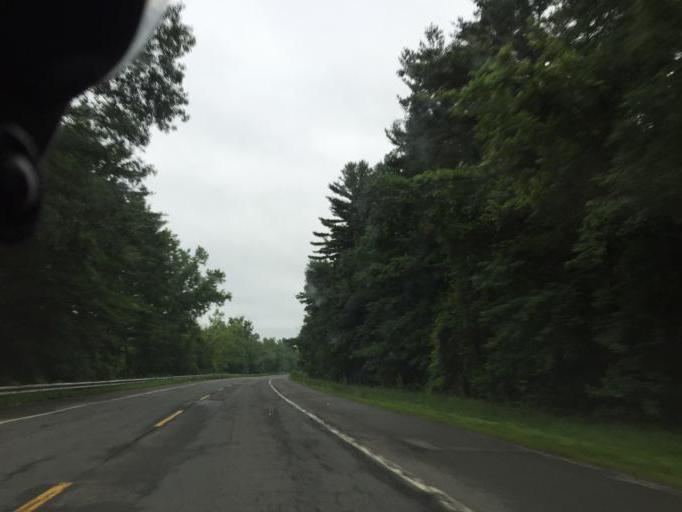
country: US
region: Massachusetts
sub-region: Berkshire County
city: Sheffield
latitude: 42.0826
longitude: -73.3385
